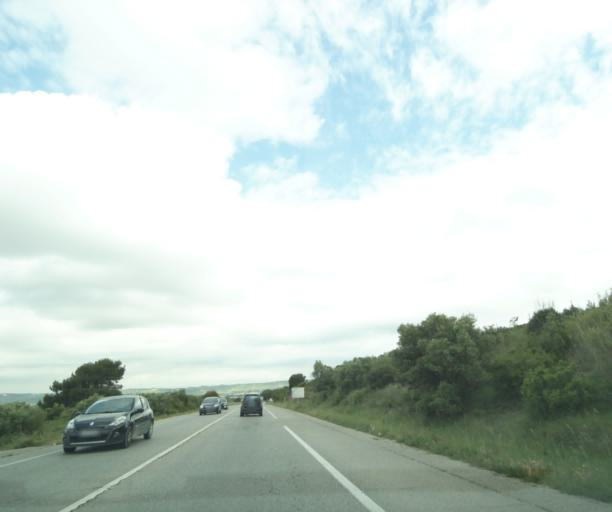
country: FR
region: Provence-Alpes-Cote d'Azur
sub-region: Departement des Bouches-du-Rhone
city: La Fare-les-Oliviers
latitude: 43.5222
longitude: 5.1980
